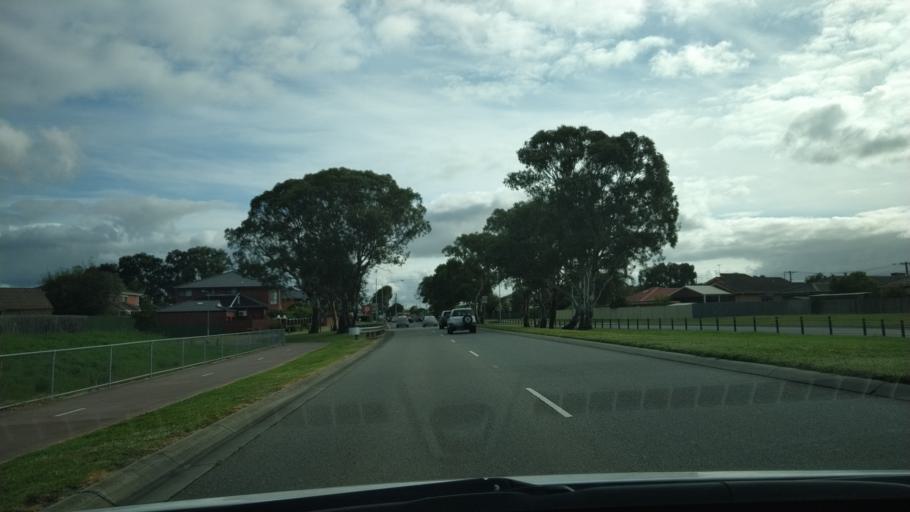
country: AU
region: Victoria
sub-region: Greater Dandenong
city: Keysborough
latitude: -37.9969
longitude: 145.1747
